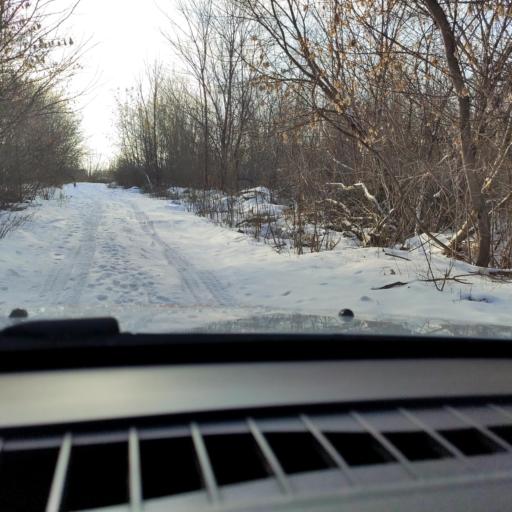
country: RU
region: Samara
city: Tol'yatti
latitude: 53.5309
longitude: 49.2572
